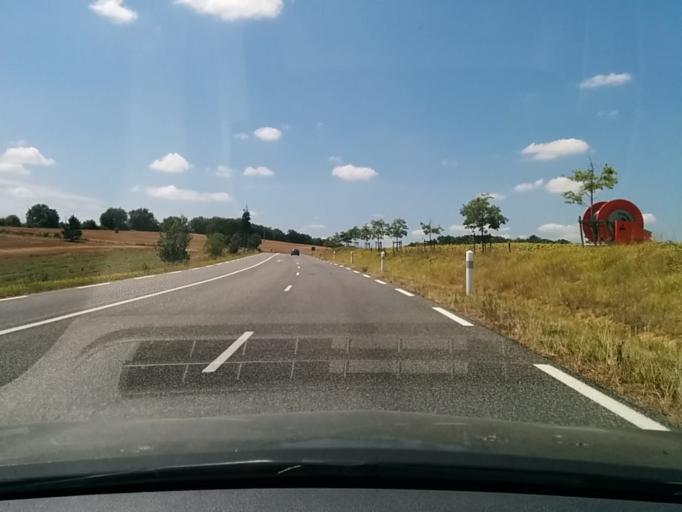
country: FR
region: Midi-Pyrenees
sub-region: Departement du Gers
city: Jegun
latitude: 43.7137
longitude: 0.4332
